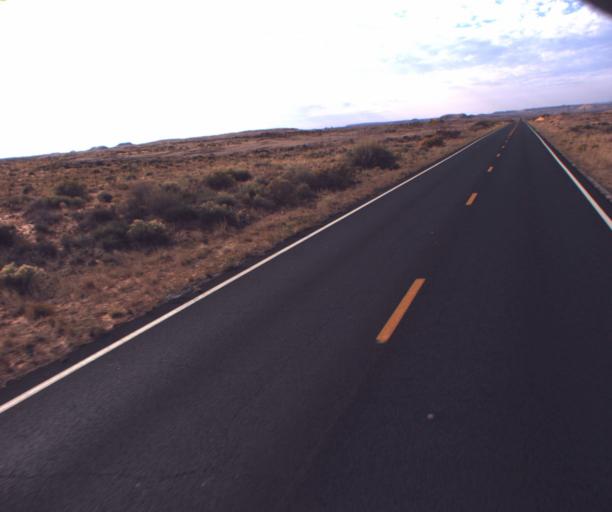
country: US
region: Arizona
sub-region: Apache County
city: Many Farms
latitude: 36.8166
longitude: -109.6461
